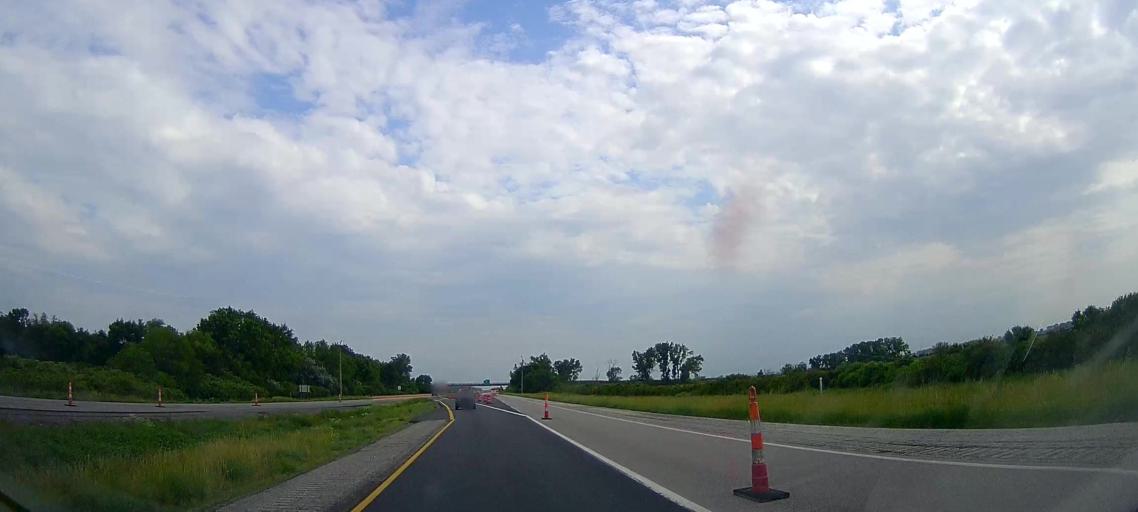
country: US
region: Nebraska
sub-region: Burt County
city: Tekamah
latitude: 41.7330
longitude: -96.0481
